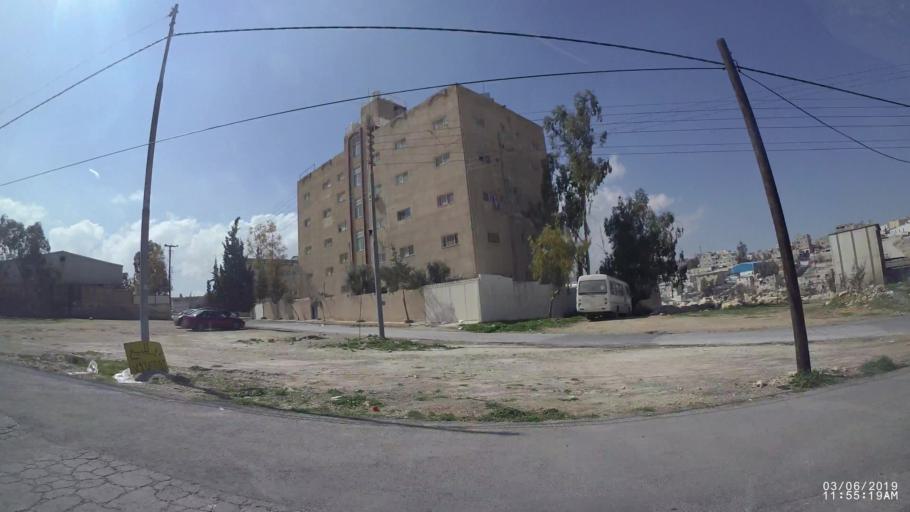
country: JO
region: Zarqa
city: Russeifa
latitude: 31.9861
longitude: 36.0095
